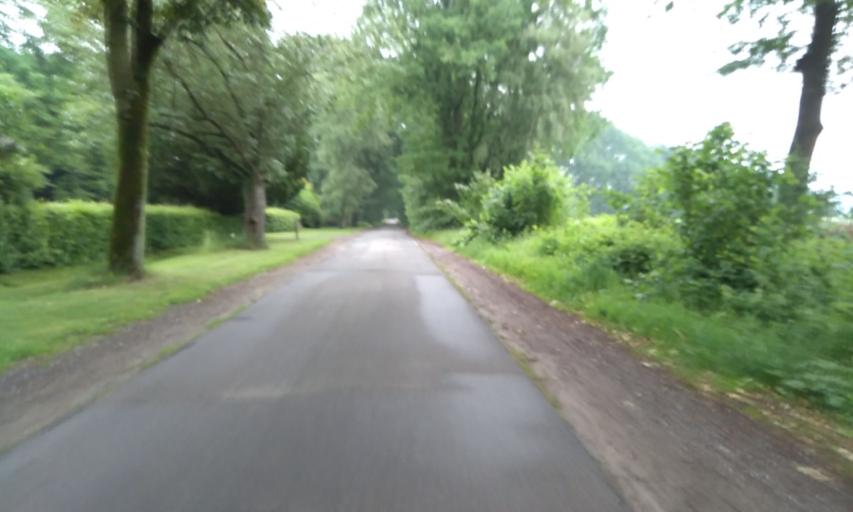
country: DE
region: Lower Saxony
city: Deinste
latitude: 53.5440
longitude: 9.4346
